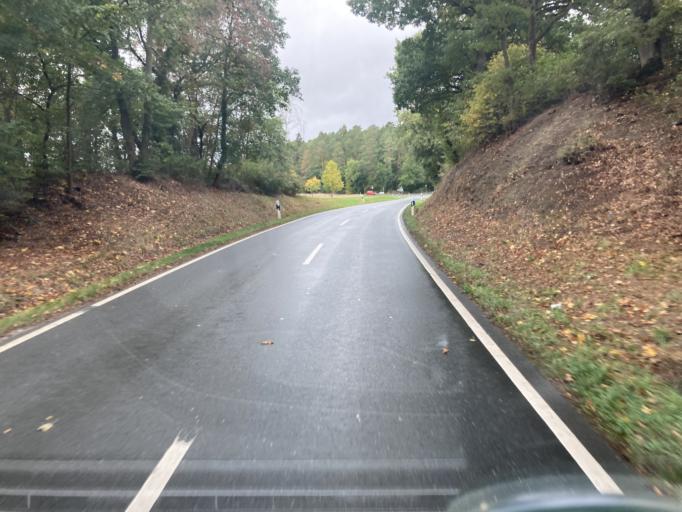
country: DE
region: Hesse
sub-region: Regierungsbezirk Darmstadt
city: Usingen
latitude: 50.3380
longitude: 8.5156
